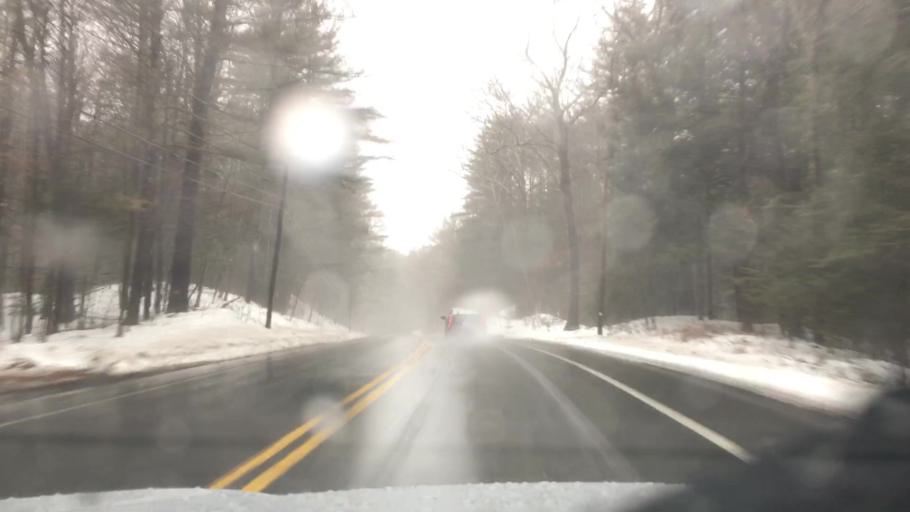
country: US
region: Massachusetts
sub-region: Franklin County
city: Orange
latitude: 42.5312
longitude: -72.3189
